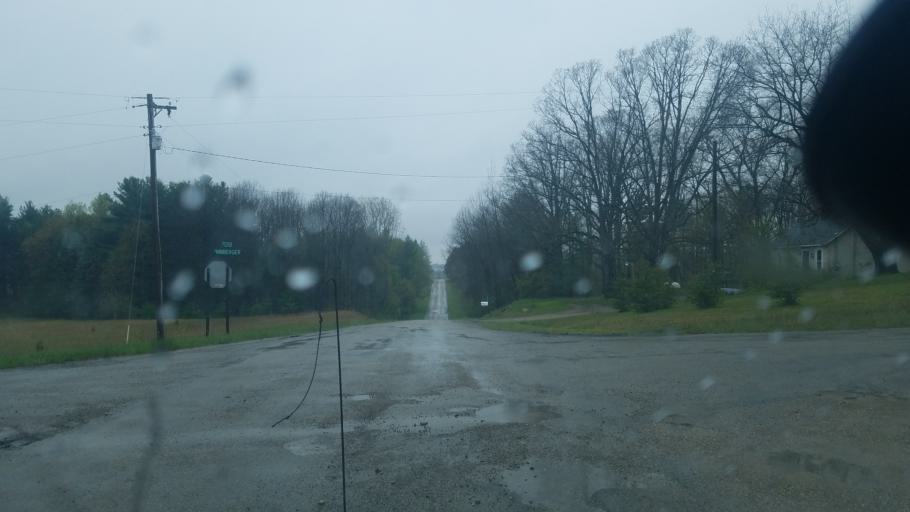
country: US
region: Michigan
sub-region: Montcalm County
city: Lakeview
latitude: 43.4531
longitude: -85.3129
